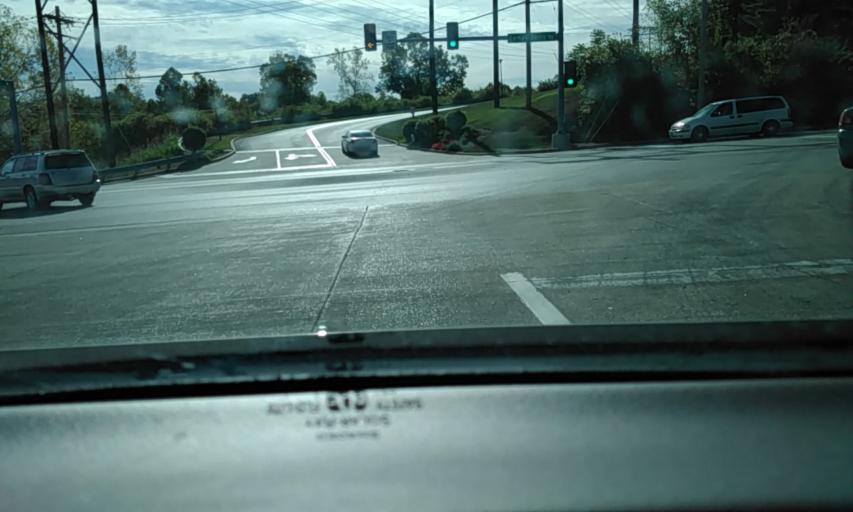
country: US
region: Missouri
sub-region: Saint Louis County
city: Mehlville
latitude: 38.4945
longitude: -90.3450
